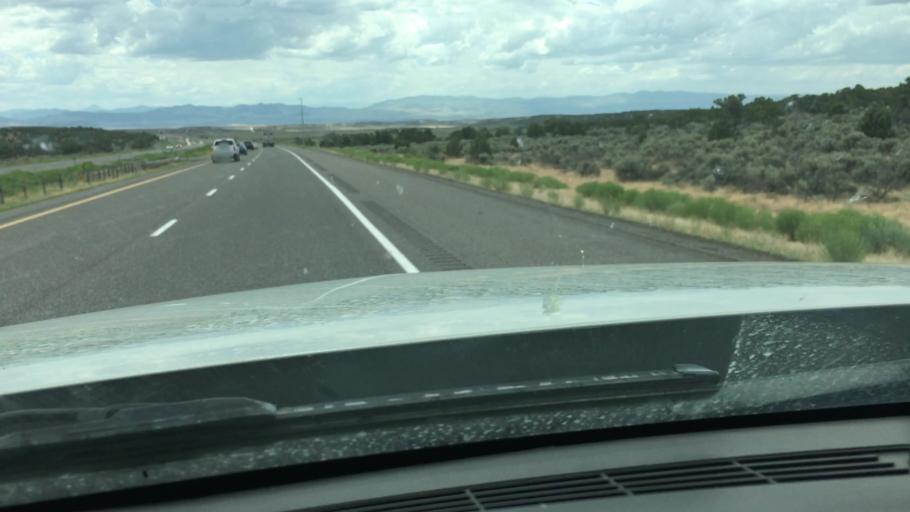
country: US
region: Utah
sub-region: Beaver County
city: Beaver
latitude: 38.3775
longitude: -112.6623
